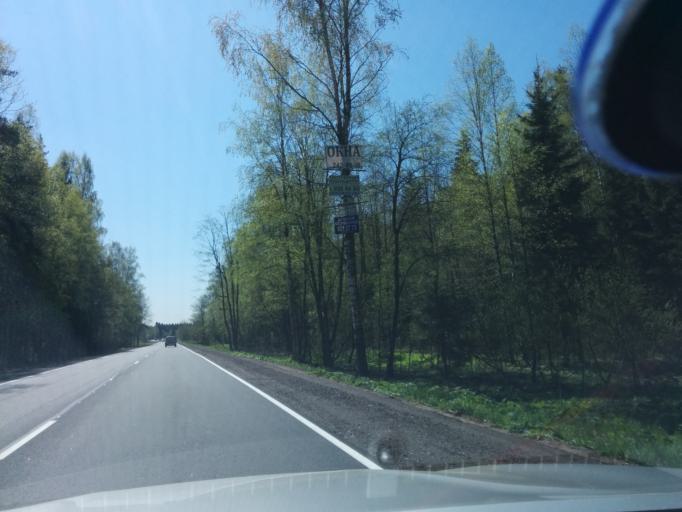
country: RU
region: Leningrad
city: Verkhniye Osel'ki
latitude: 60.2076
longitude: 30.4265
